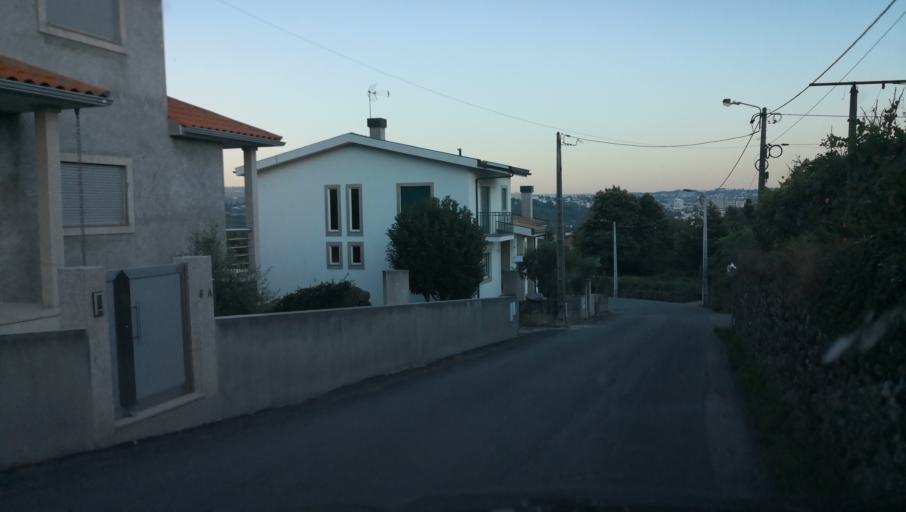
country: PT
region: Vila Real
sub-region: Vila Real
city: Vila Real
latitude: 41.3169
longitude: -7.7679
